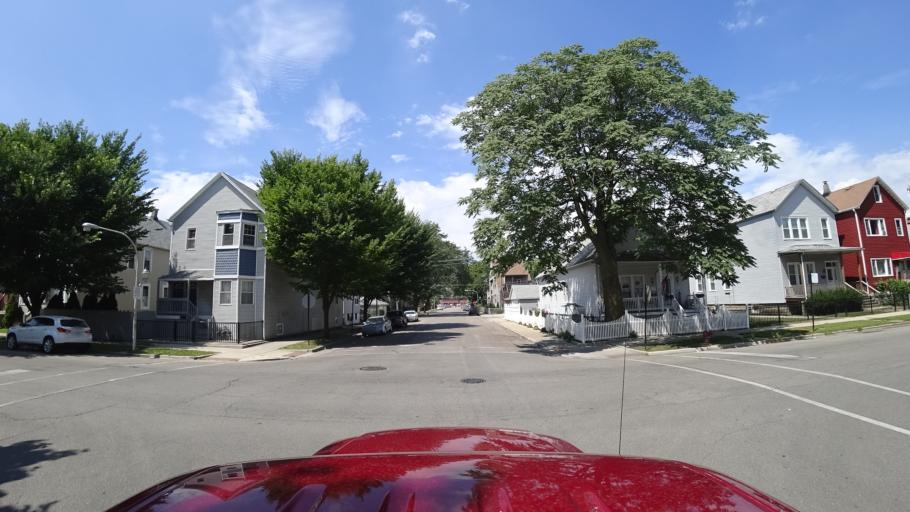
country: US
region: Illinois
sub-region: Cook County
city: Chicago
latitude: 41.8107
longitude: -87.6431
